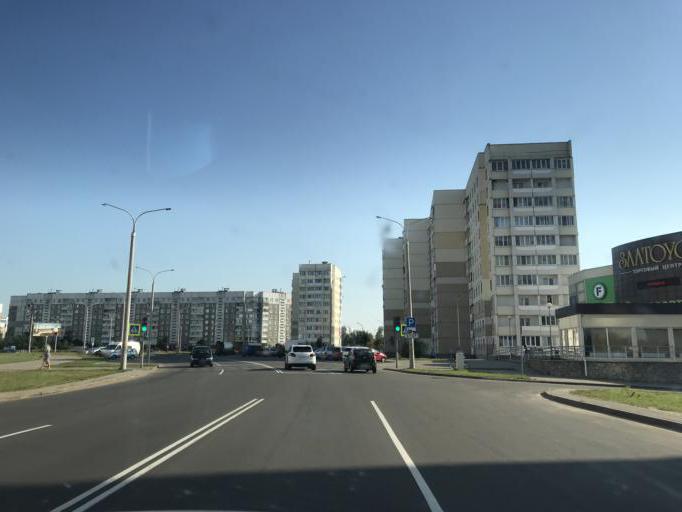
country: BY
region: Mogilev
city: Mahilyow
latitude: 53.8814
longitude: 30.3570
